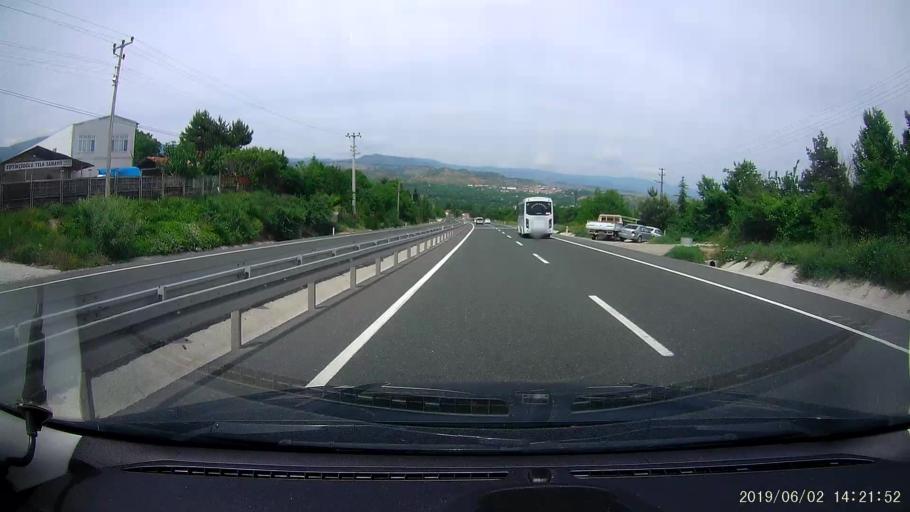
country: TR
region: Kastamonu
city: Tosya
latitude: 40.9847
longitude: 34.0076
